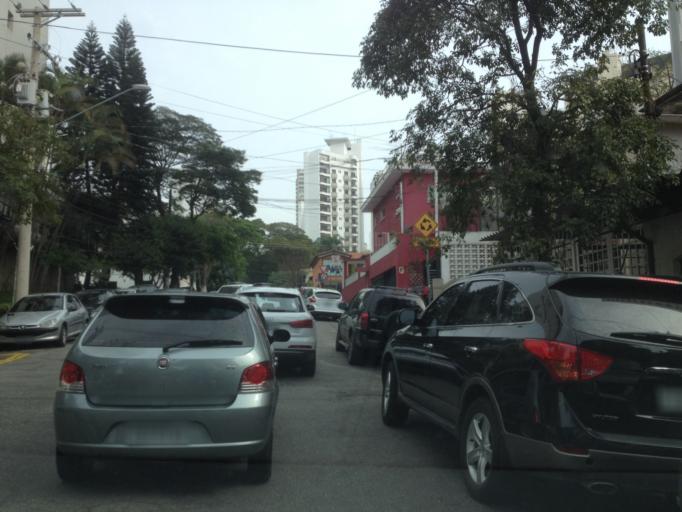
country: BR
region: Sao Paulo
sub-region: Diadema
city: Diadema
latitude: -23.6231
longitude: -46.6714
